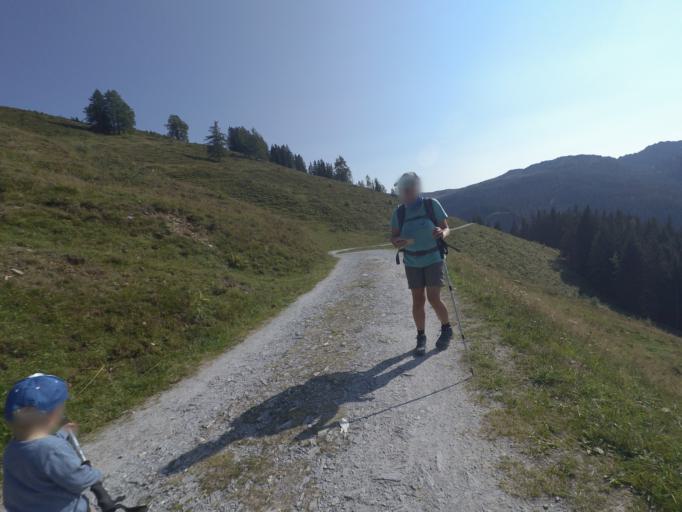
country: AT
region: Salzburg
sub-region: Politischer Bezirk Sankt Johann im Pongau
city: Kleinarl
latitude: 47.2777
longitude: 13.2571
